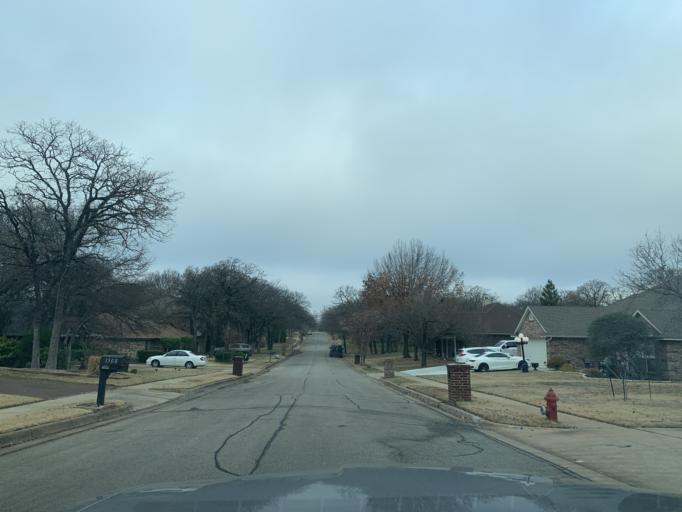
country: US
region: Texas
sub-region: Tarrant County
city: Bedford
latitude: 32.8317
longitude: -97.1453
